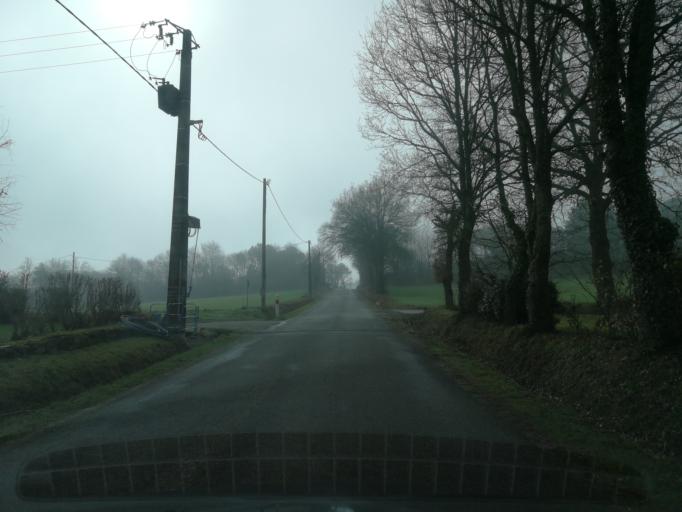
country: FR
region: Brittany
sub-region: Departement du Morbihan
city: La Vraie-Croix
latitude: 47.7195
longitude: -2.5124
